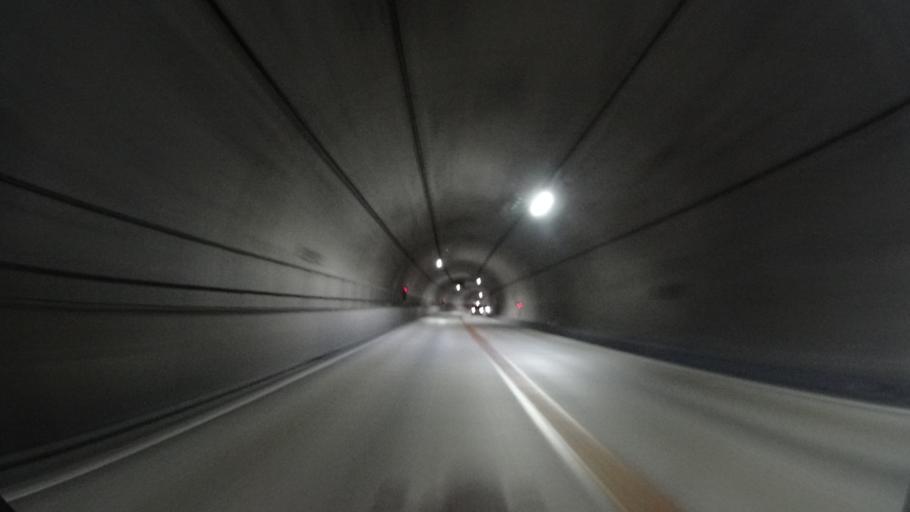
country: JP
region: Mie
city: Ueno-ebisumachi
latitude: 34.7715
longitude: 135.9826
